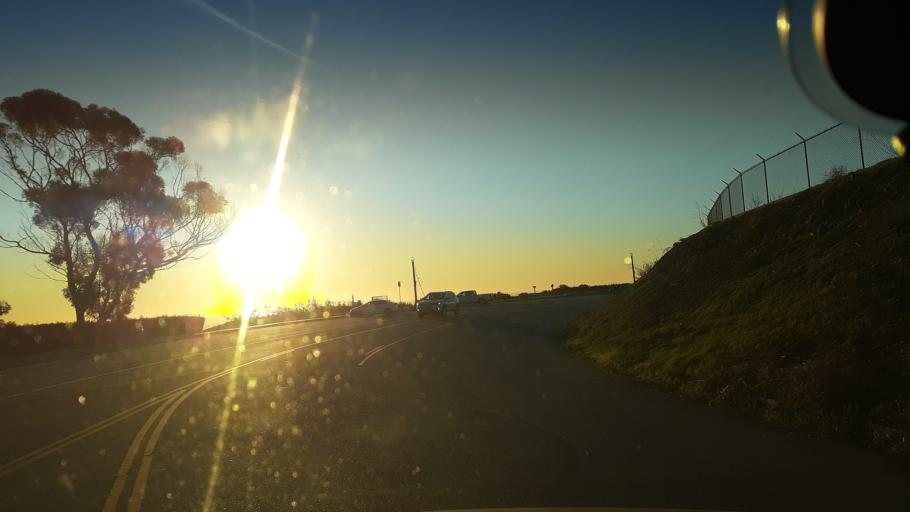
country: US
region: California
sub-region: Los Angeles County
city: San Pedro
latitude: 33.7131
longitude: -118.2928
